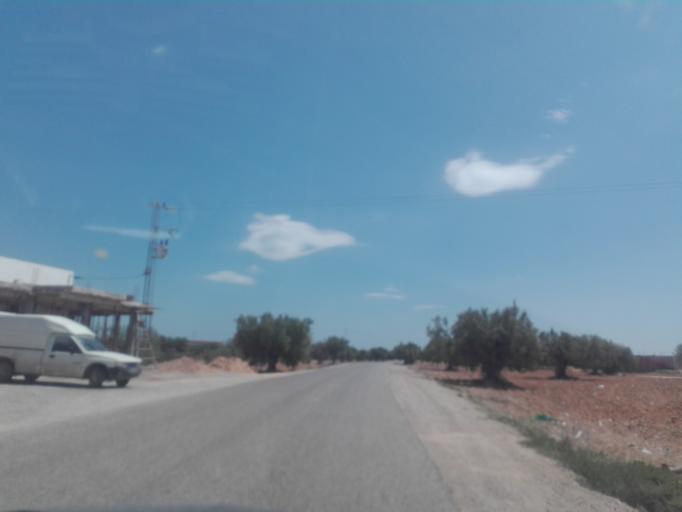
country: TN
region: Safaqis
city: Sfax
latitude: 34.6244
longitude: 10.6046
